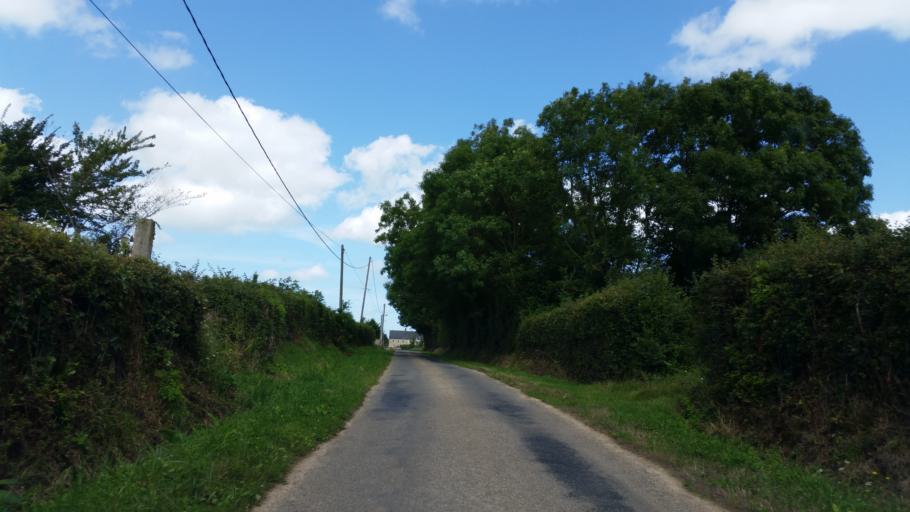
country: FR
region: Lower Normandy
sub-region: Departement de la Manche
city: Montebourg
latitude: 49.4566
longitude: -1.3450
